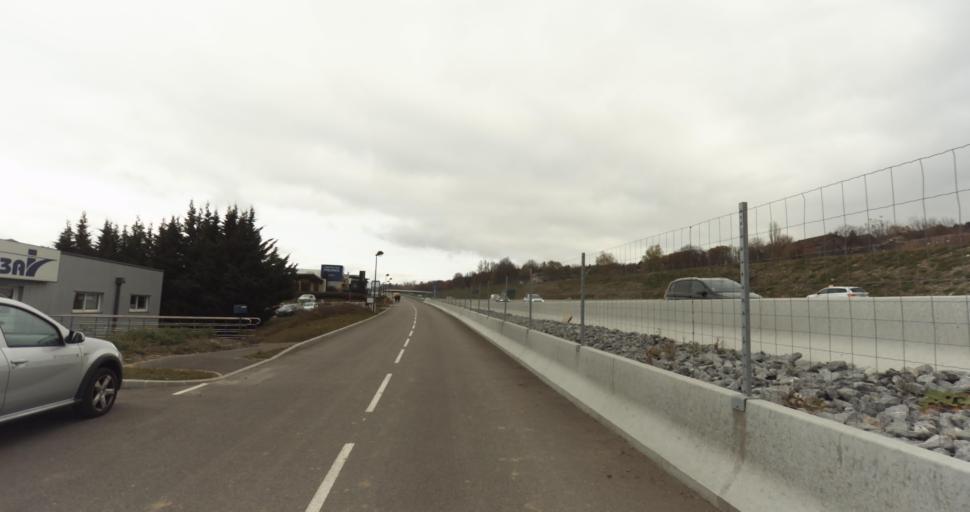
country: FR
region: Rhone-Alpes
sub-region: Departement de la Haute-Savoie
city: Pringy
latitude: 45.9684
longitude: 6.1310
